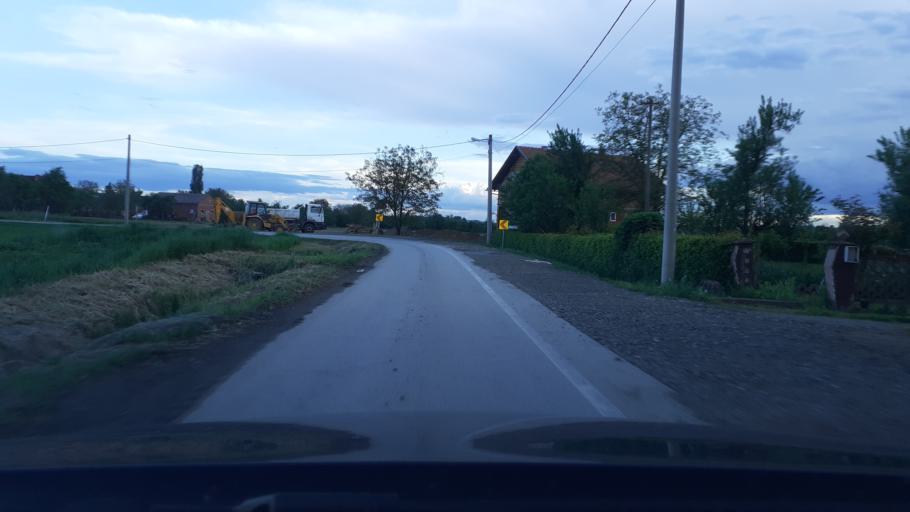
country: HR
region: Pozesko-Slavonska
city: Gradac
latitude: 45.3162
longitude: 17.8112
